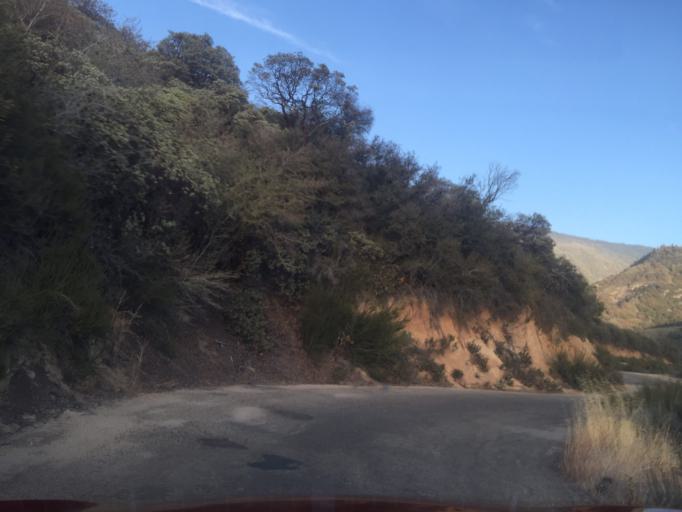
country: US
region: California
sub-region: Tulare County
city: Three Rivers
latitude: 36.4302
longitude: -118.7502
